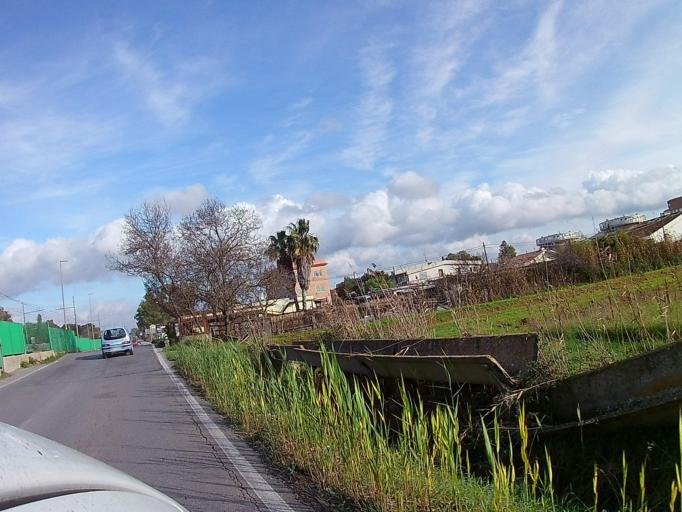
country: IT
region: Latium
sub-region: Citta metropolitana di Roma Capitale
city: Acilia-Castel Fusano-Ostia Antica
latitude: 41.7621
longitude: 12.3112
